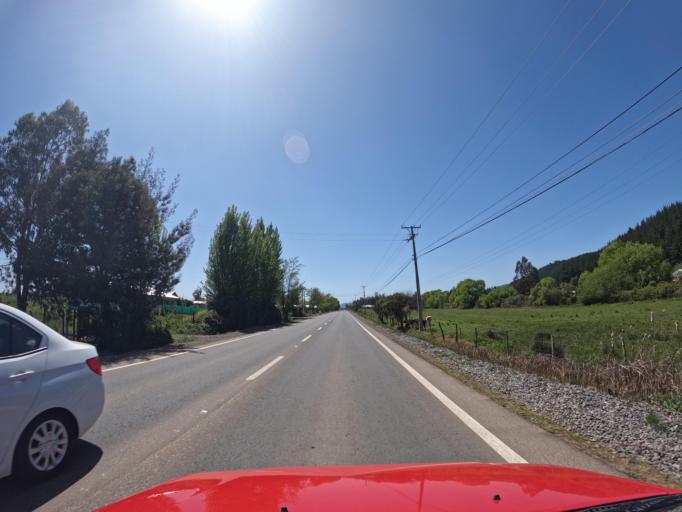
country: CL
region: Maule
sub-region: Provincia de Linares
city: Colbun
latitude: -35.7292
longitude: -71.4195
